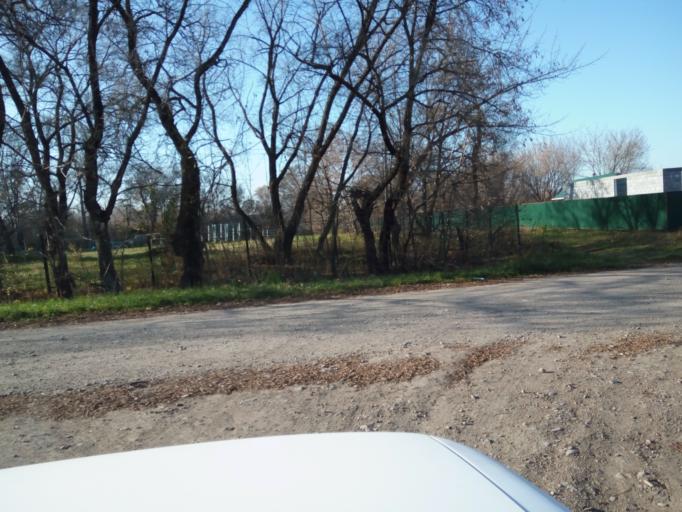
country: RU
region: Primorskiy
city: Lazo
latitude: 45.8777
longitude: 133.6438
